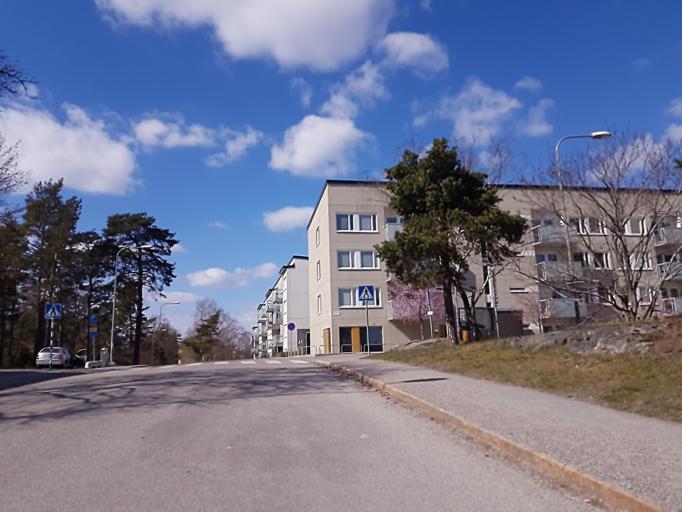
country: SE
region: Stockholm
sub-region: Nacka Kommun
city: Nacka
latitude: 59.2847
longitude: 18.1119
